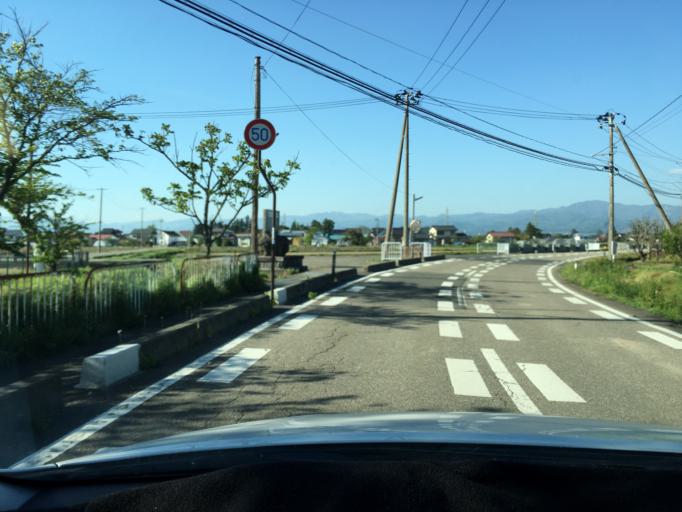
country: JP
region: Fukushima
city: Kitakata
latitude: 37.5699
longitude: 139.8739
